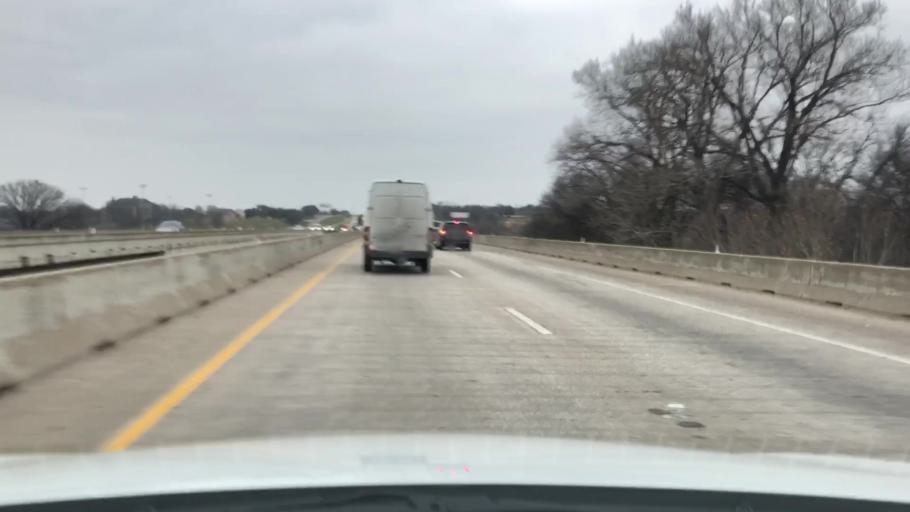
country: US
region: Texas
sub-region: Denton County
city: Sanger
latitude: 33.3379
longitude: -97.1812
